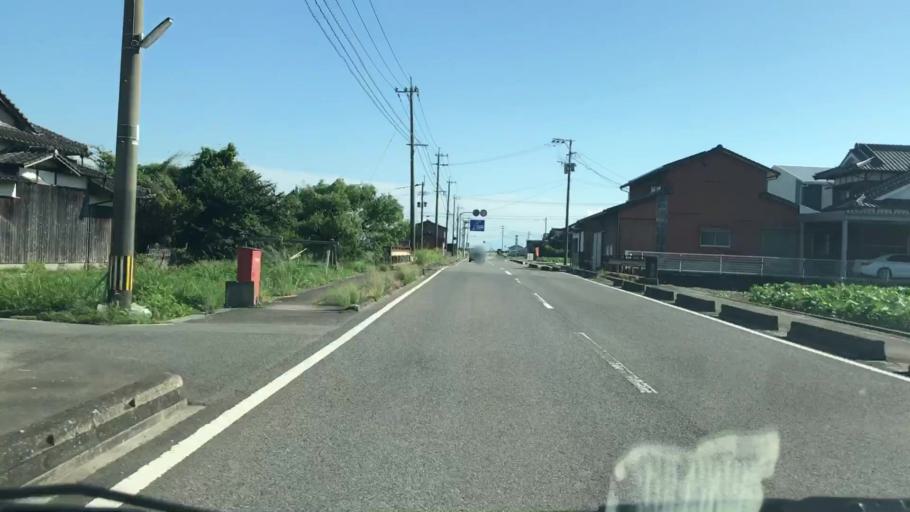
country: JP
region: Saga Prefecture
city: Okawa
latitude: 33.1997
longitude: 130.3351
